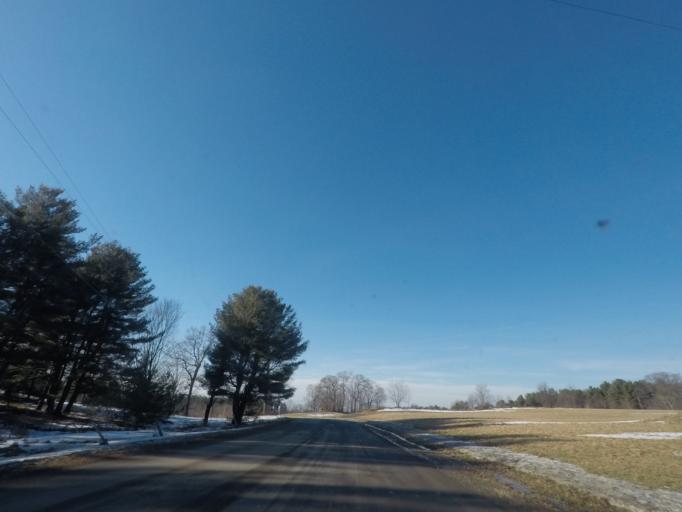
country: US
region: New York
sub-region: Rensselaer County
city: Averill Park
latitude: 42.6305
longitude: -73.5120
